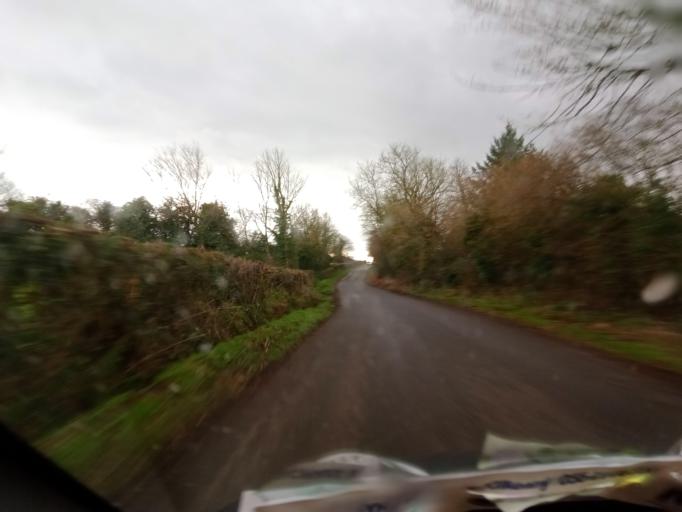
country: IE
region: Munster
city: Fethard
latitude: 52.5460
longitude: -7.7613
